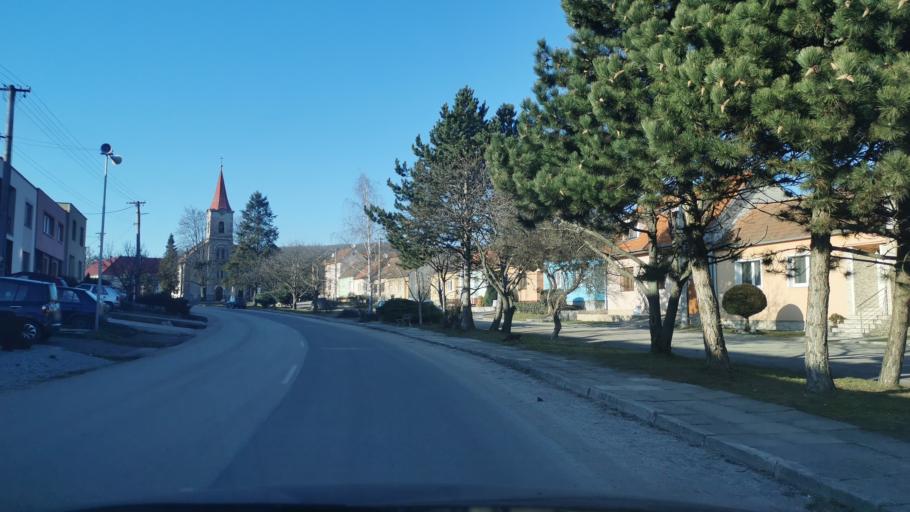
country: SK
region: Trnavsky
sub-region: Okres Senica
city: Senica
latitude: 48.7471
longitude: 17.3539
